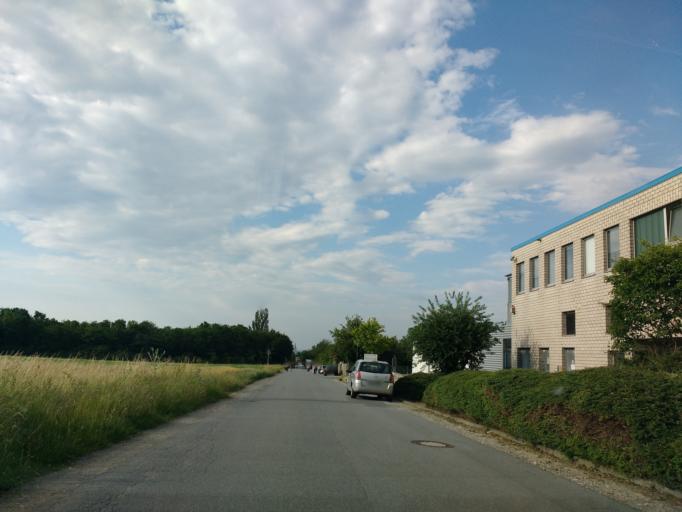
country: DE
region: North Rhine-Westphalia
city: Geseke
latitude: 51.6257
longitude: 8.5057
